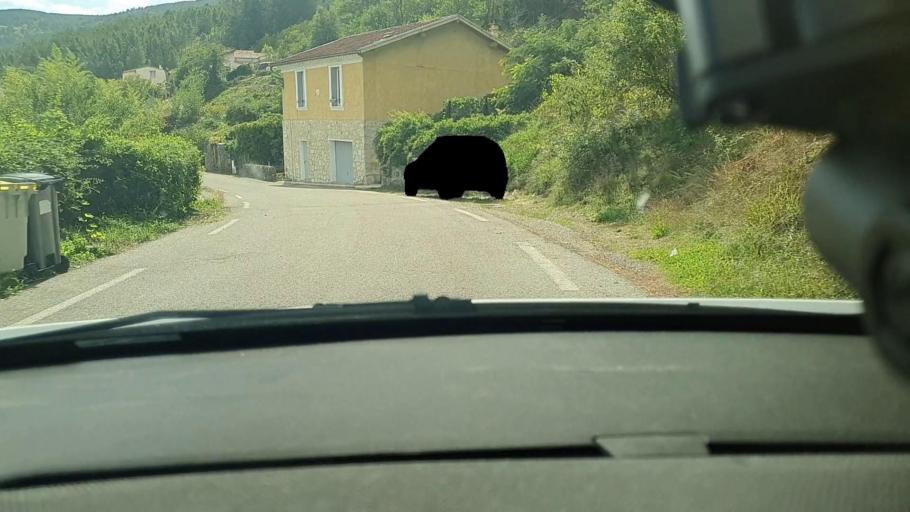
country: FR
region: Languedoc-Roussillon
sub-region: Departement du Gard
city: Branoux-les-Taillades
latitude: 44.2908
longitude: 4.0080
